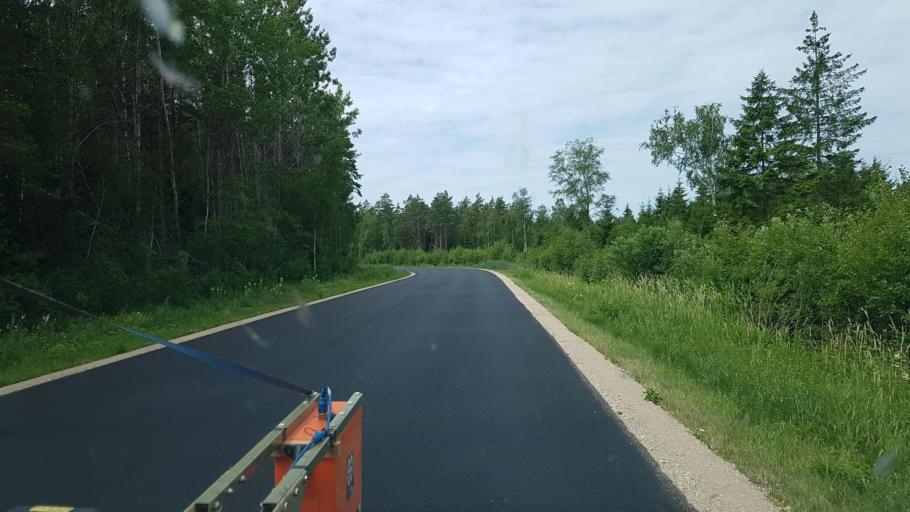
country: EE
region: Paernumaa
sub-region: Audru vald
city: Audru
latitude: 58.6207
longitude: 24.2352
